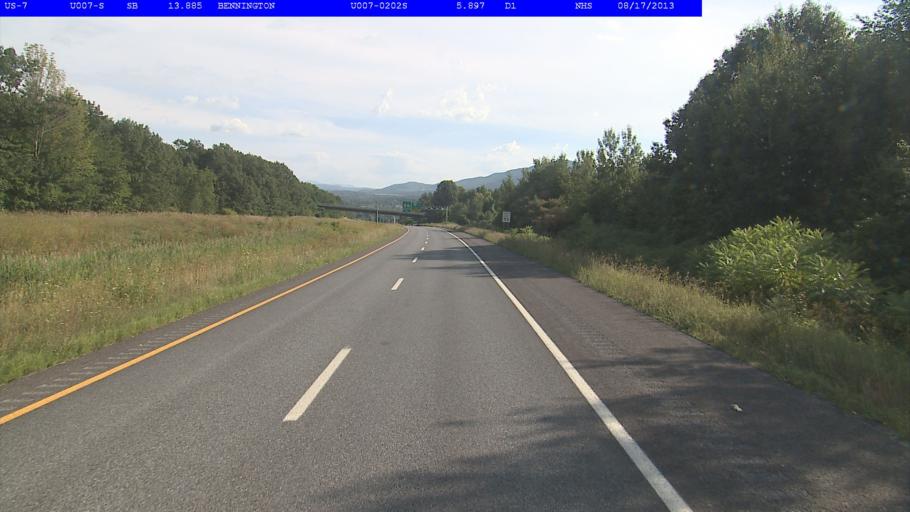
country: US
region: Vermont
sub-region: Bennington County
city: North Bennington
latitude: 42.9175
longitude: -73.2085
